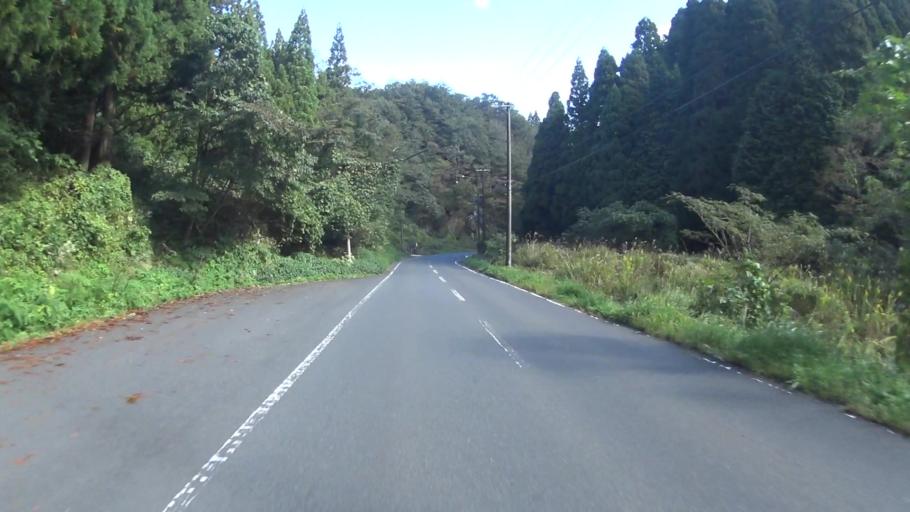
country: JP
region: Kyoto
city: Miyazu
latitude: 35.6337
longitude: 135.1239
